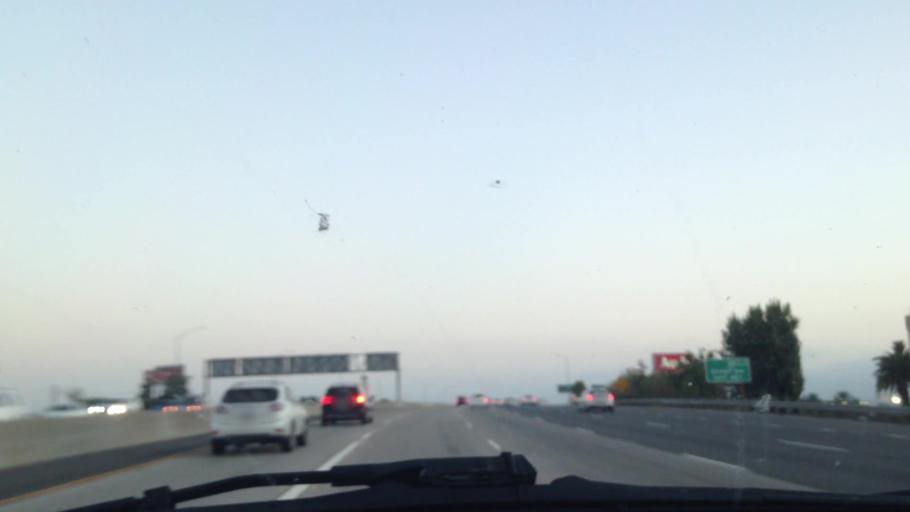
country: US
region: California
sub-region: Orange County
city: Tustin
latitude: 33.7299
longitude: -117.8340
